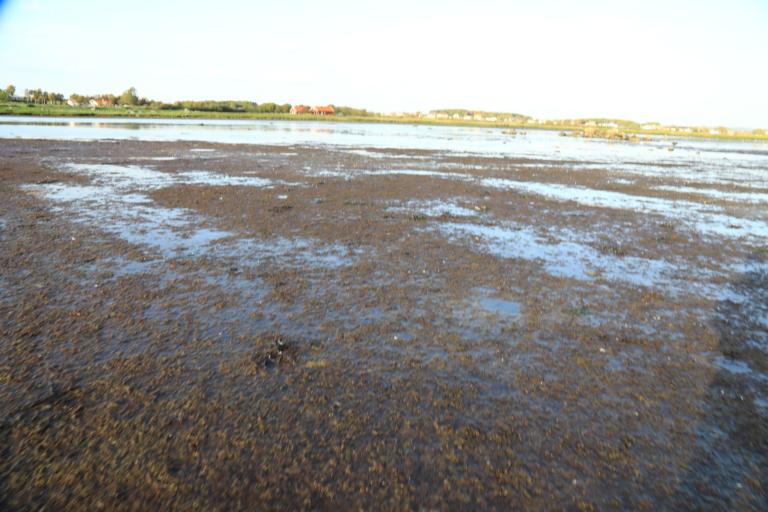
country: SE
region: Halland
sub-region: Varbergs Kommun
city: Traslovslage
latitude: 57.0331
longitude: 12.3060
